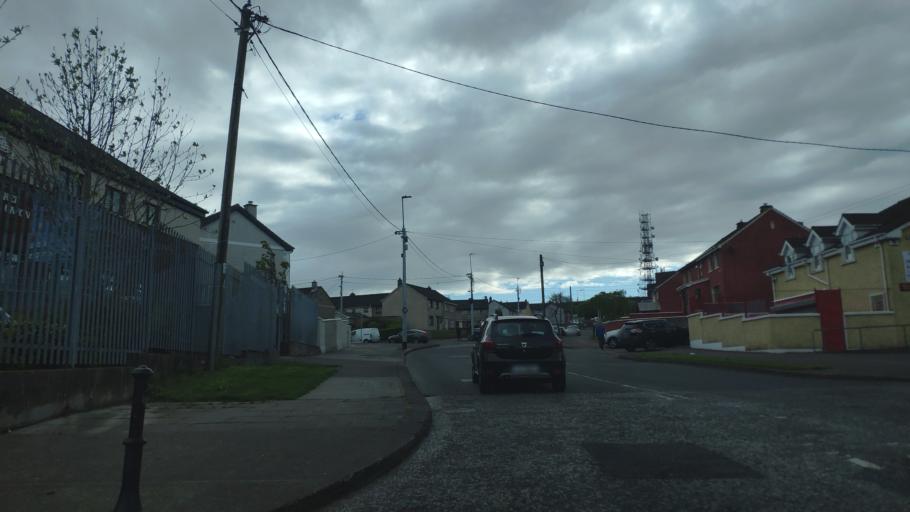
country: IE
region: Munster
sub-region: County Cork
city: Cork
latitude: 51.9148
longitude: -8.4849
